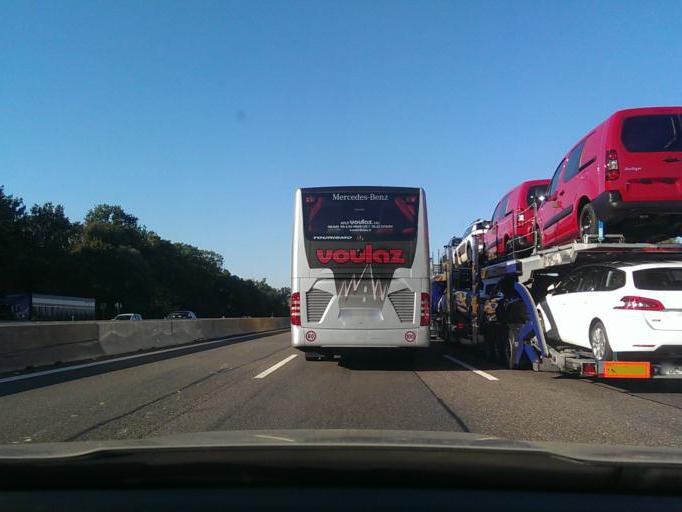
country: DE
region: Baden-Wuerttemberg
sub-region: Karlsruhe Region
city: Karlsruhe
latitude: 48.9772
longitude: 8.4372
